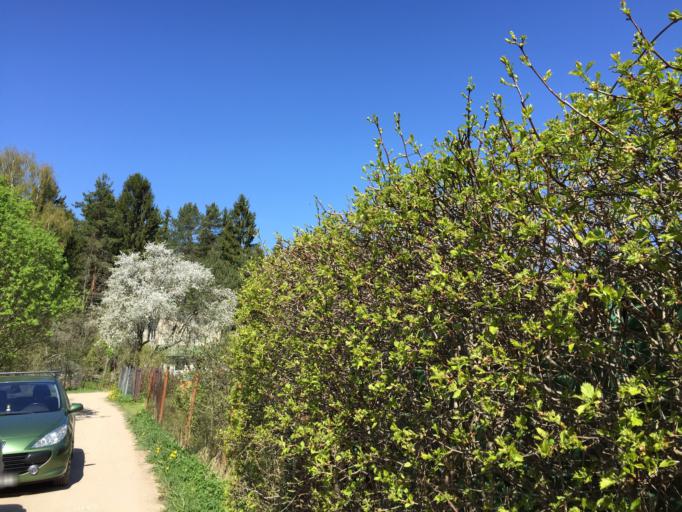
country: LV
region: Saulkrastu
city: Saulkrasti
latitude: 57.3164
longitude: 24.4369
